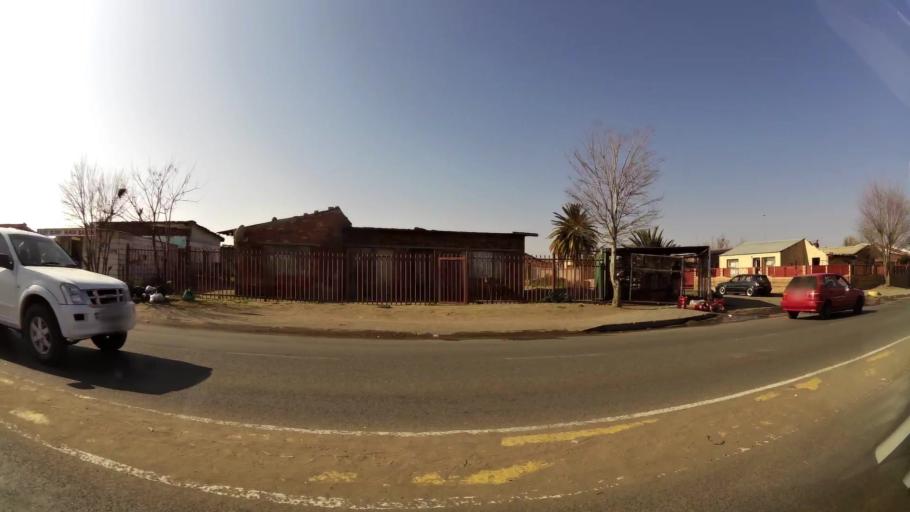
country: ZA
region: Orange Free State
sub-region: Mangaung Metropolitan Municipality
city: Bloemfontein
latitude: -29.1464
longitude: 26.2408
